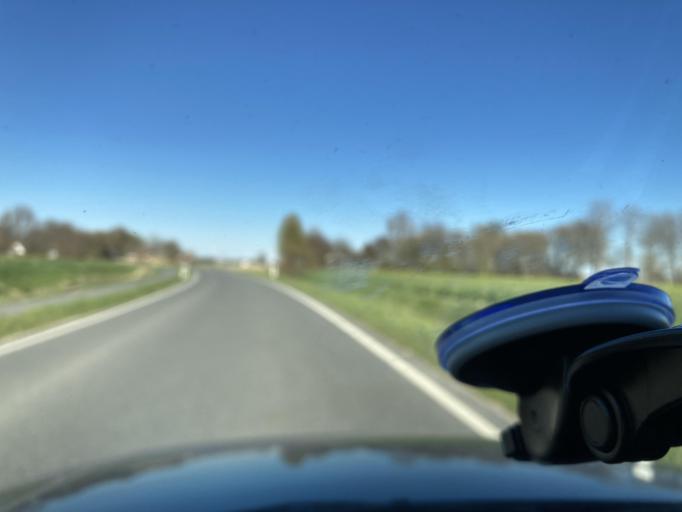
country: DE
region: Schleswig-Holstein
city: Neuenkirchen
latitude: 54.2310
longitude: 8.9692
